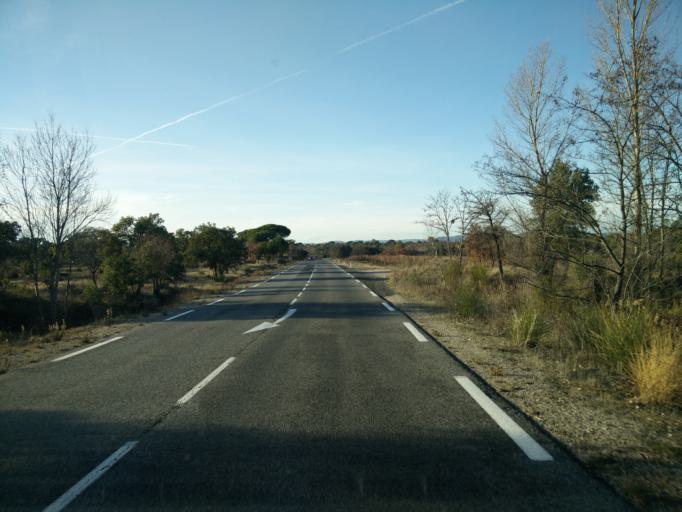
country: FR
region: Provence-Alpes-Cote d'Azur
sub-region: Departement du Var
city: La Garde-Freinet
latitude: 43.3533
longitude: 6.4168
